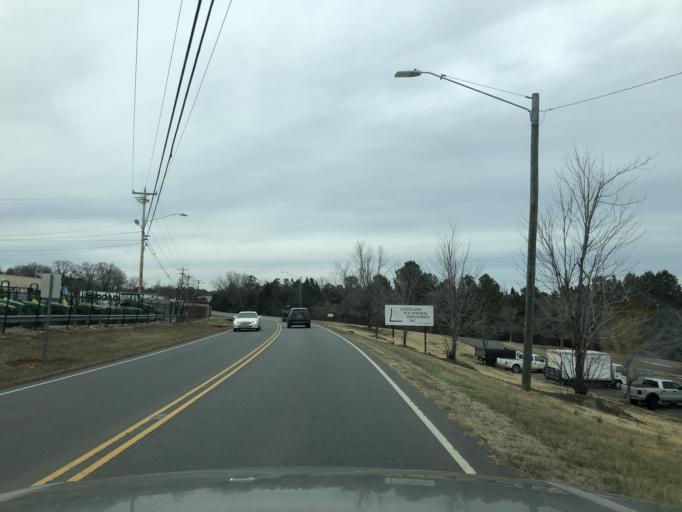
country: US
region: North Carolina
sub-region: Cleveland County
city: Shelby
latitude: 35.2980
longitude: -81.4857
